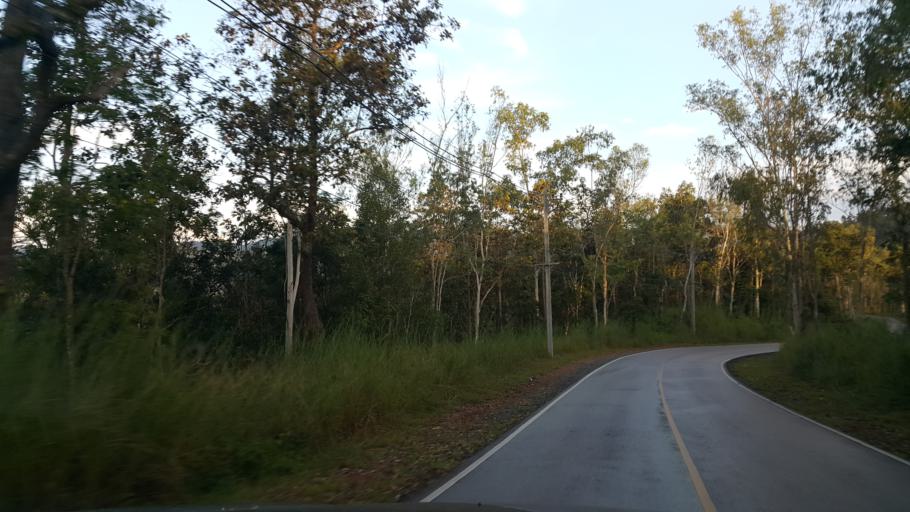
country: TH
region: Chiang Mai
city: Mae On
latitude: 18.7192
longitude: 99.2923
